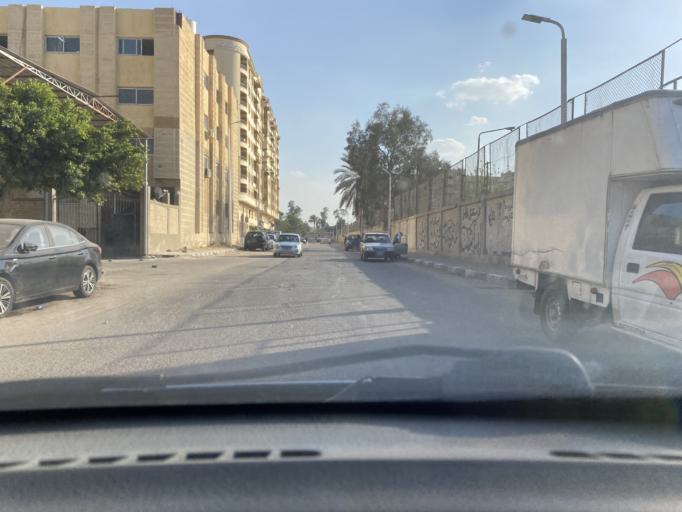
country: EG
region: Muhafazat al Qahirah
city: Cairo
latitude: 30.1045
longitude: 31.3044
